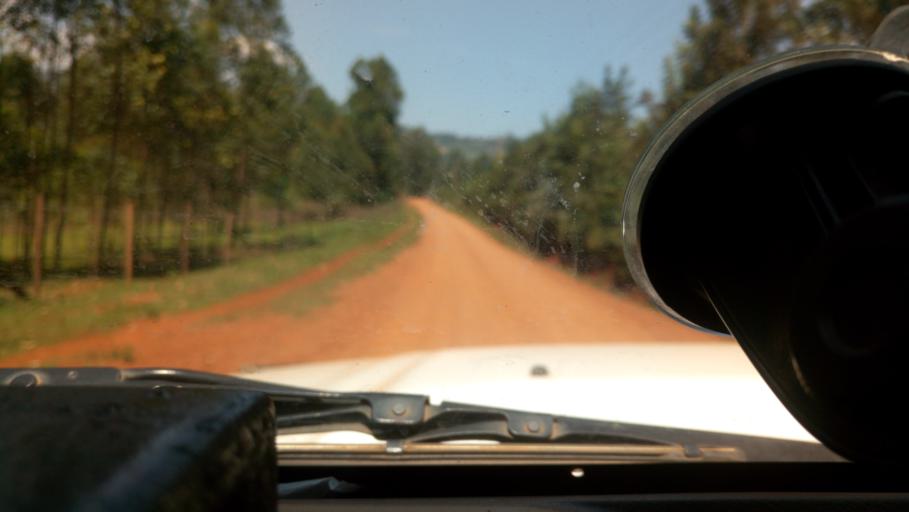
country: KE
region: Kisii
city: Ogembo
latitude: -0.7870
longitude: 34.7951
